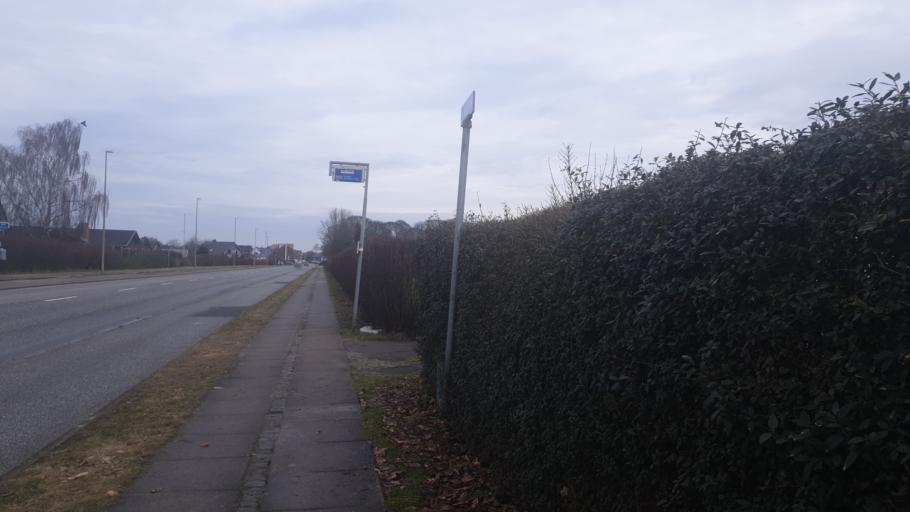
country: DK
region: Central Jutland
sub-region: Hedensted Kommune
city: Hedensted
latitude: 55.7662
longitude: 9.6904
